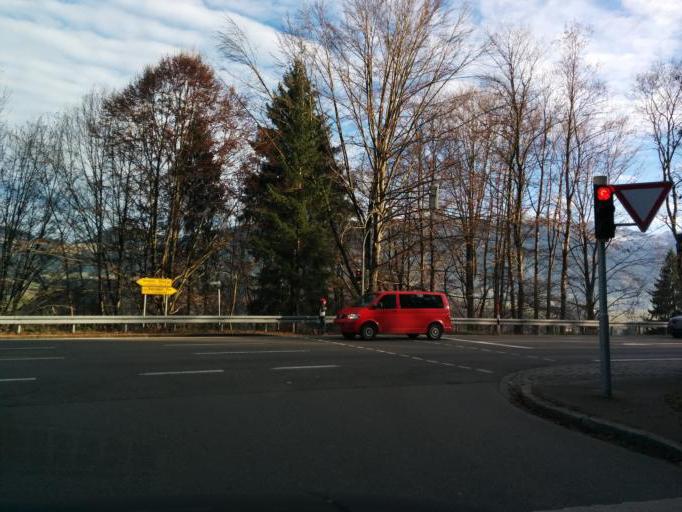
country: DE
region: Bavaria
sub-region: Swabia
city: Ofterschwang
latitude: 47.4835
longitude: 10.2660
